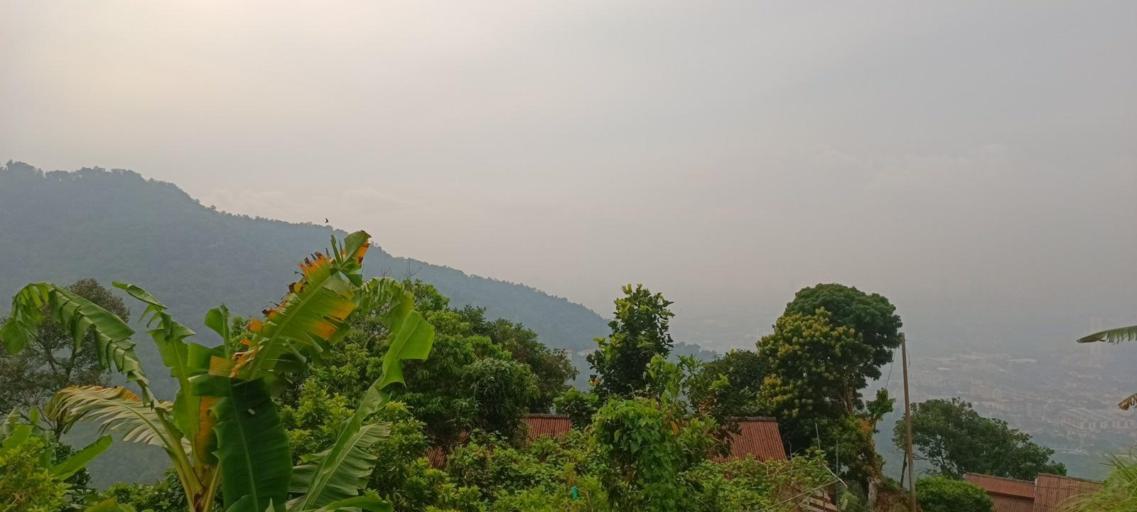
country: MY
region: Penang
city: Tanjung Tokong
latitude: 5.4173
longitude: 100.2744
